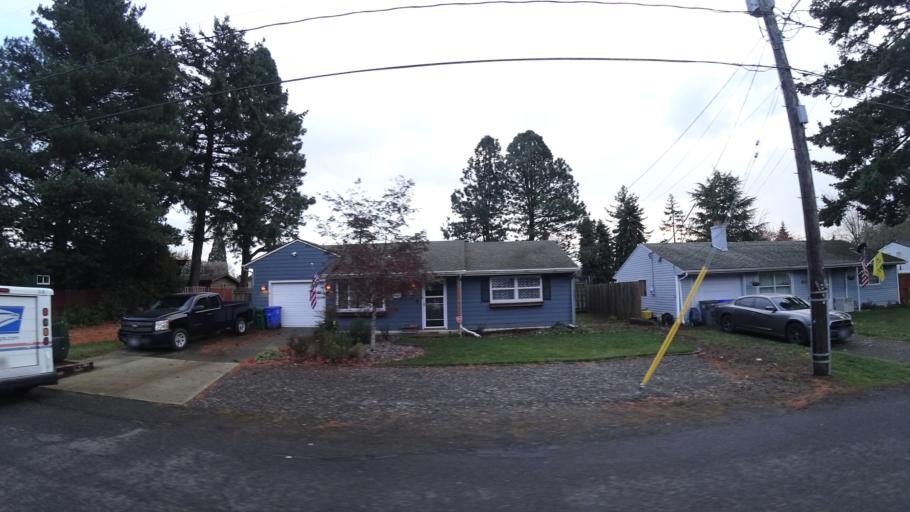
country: US
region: Oregon
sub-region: Multnomah County
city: Lents
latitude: 45.5295
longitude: -122.5354
